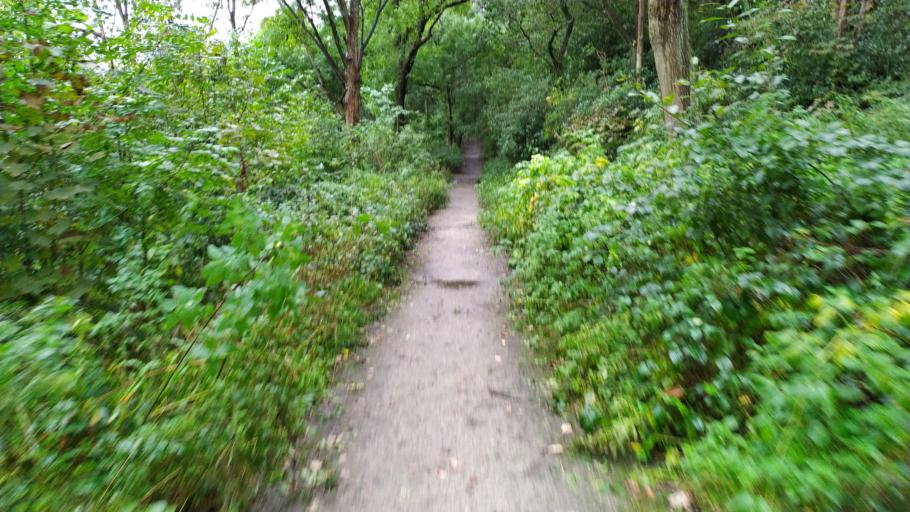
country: GB
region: England
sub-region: City and Borough of Leeds
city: Chapel Allerton
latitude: 53.8207
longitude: -1.5643
